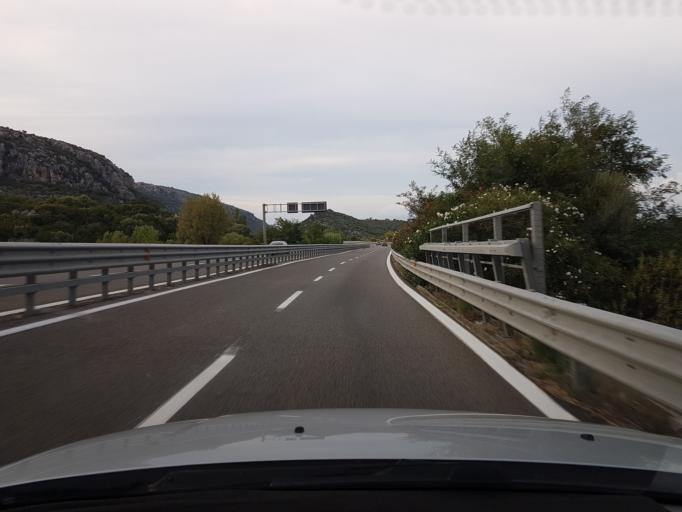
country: IT
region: Sardinia
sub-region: Provincia di Nuoro
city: Siniscola
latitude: 40.5871
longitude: 9.6918
